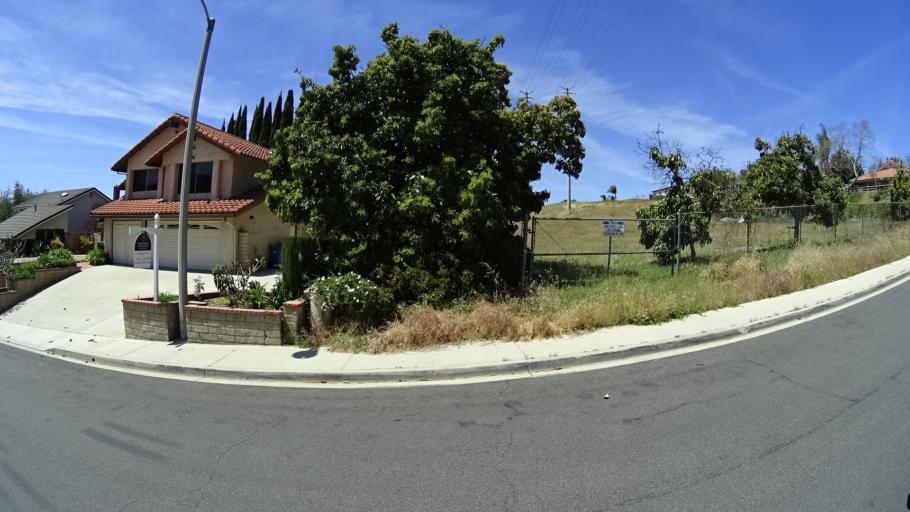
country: US
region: California
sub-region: Ventura County
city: Thousand Oaks
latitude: 34.2293
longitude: -118.8552
